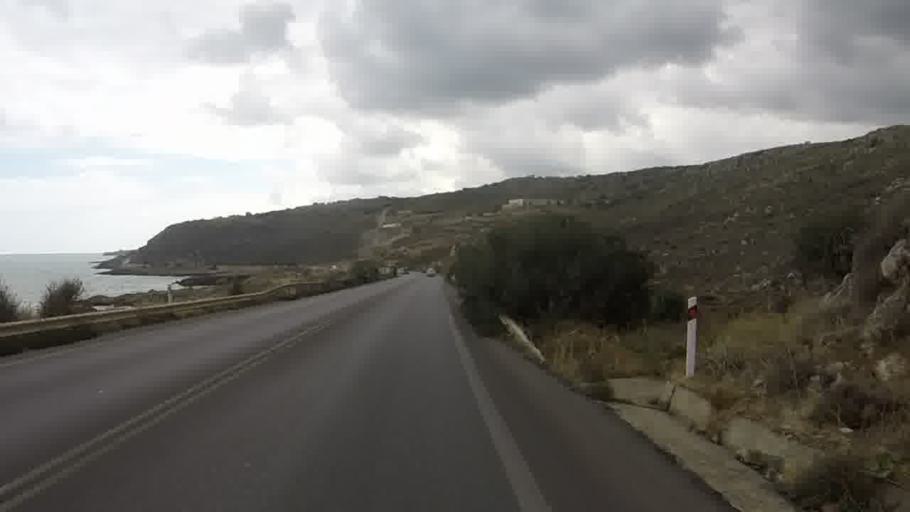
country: GR
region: Crete
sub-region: Nomos Rethymnis
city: Atsipopoulon
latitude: 35.3598
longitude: 24.3864
